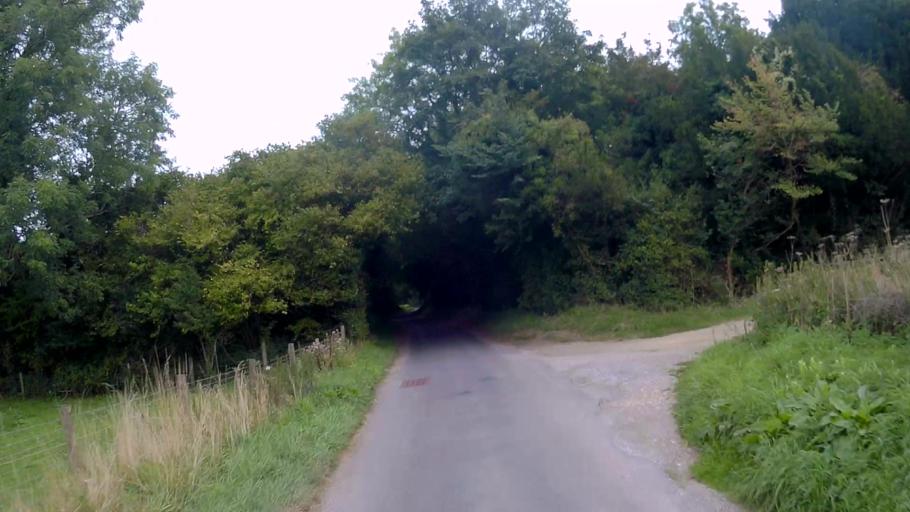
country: GB
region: England
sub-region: Hampshire
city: Kings Worthy
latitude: 51.1683
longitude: -1.3465
